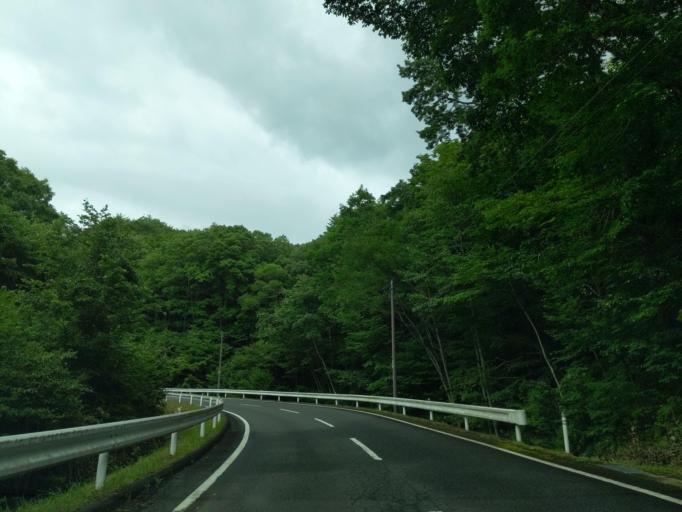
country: JP
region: Tochigi
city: Kuroiso
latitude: 37.2506
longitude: 140.0783
